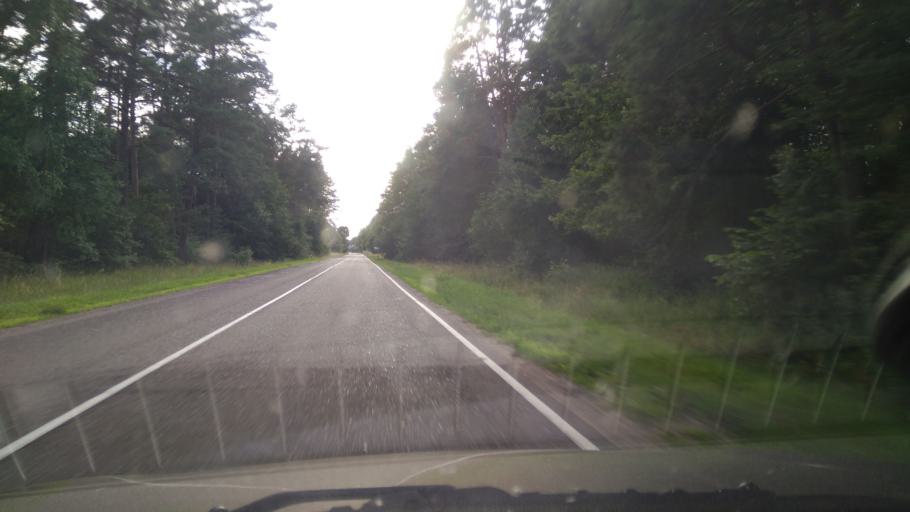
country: BY
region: Grodnenskaya
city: Masty
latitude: 53.3484
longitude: 24.6515
